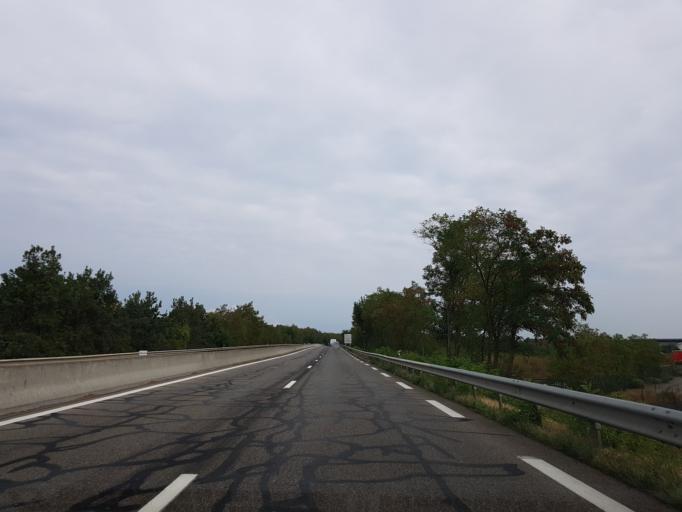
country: FR
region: Alsace
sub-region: Departement du Haut-Rhin
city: Bollwiller
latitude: 47.8412
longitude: 7.2770
